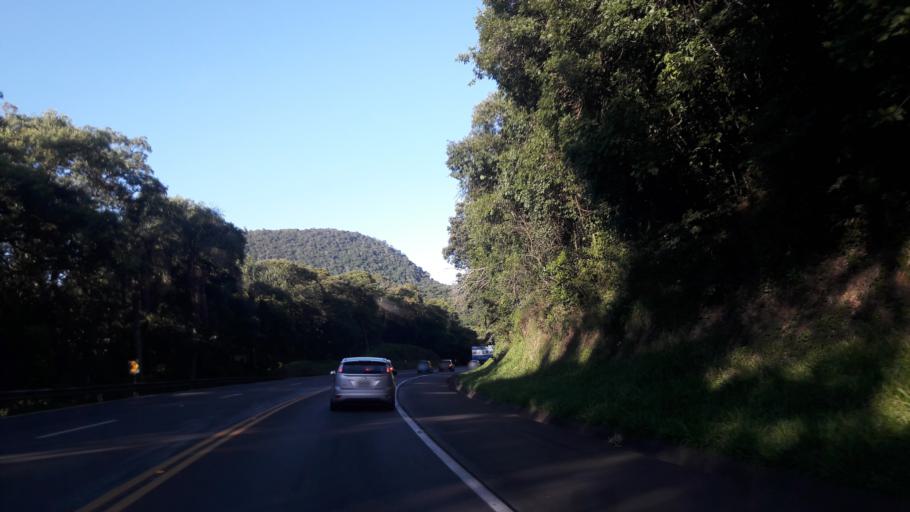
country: BR
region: Parana
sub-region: Prudentopolis
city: Prudentopolis
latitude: -25.3138
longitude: -51.1880
